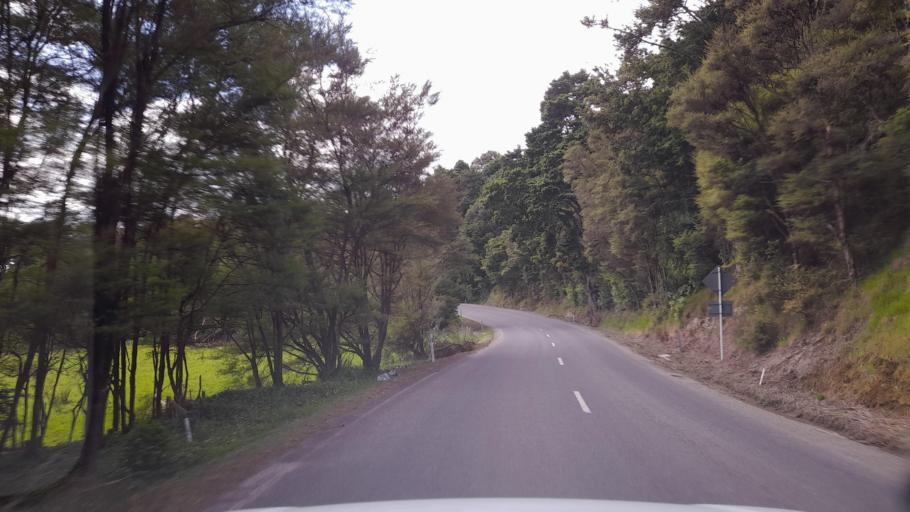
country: NZ
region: Northland
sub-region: Whangarei
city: Maungatapere
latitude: -35.6699
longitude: 174.0397
